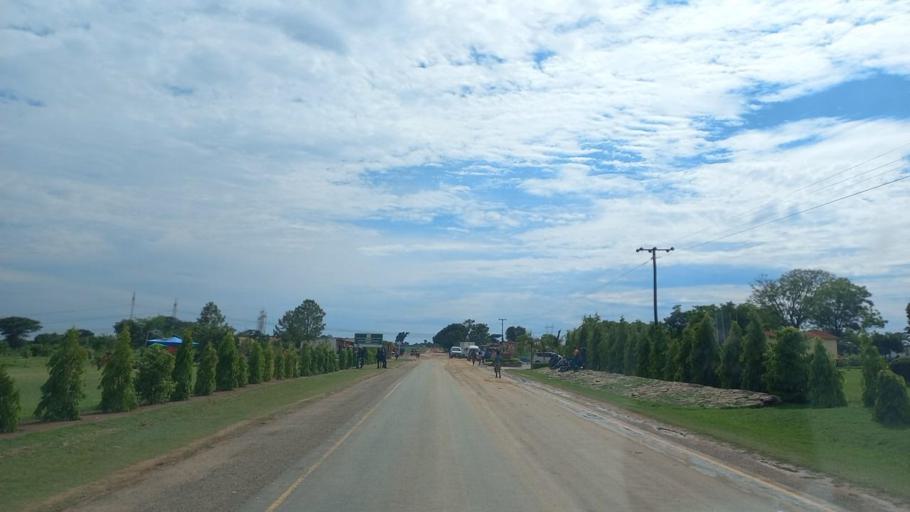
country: ZM
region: Copperbelt
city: Kitwe
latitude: -12.8719
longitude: 28.3393
